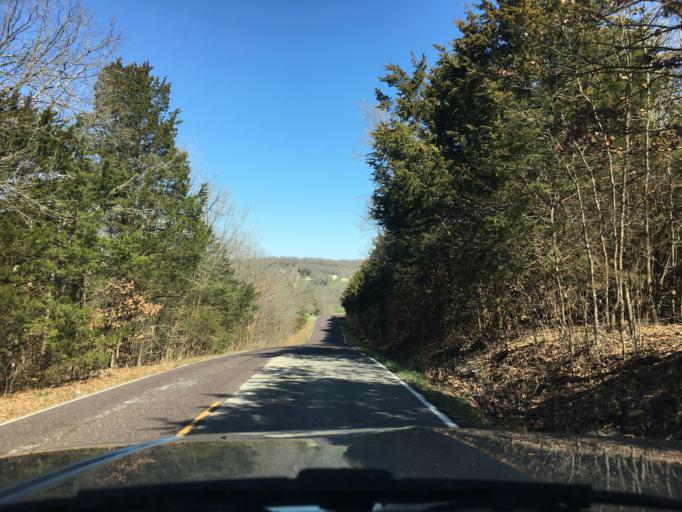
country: US
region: Missouri
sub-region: Franklin County
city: Gerald
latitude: 38.5223
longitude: -91.3293
